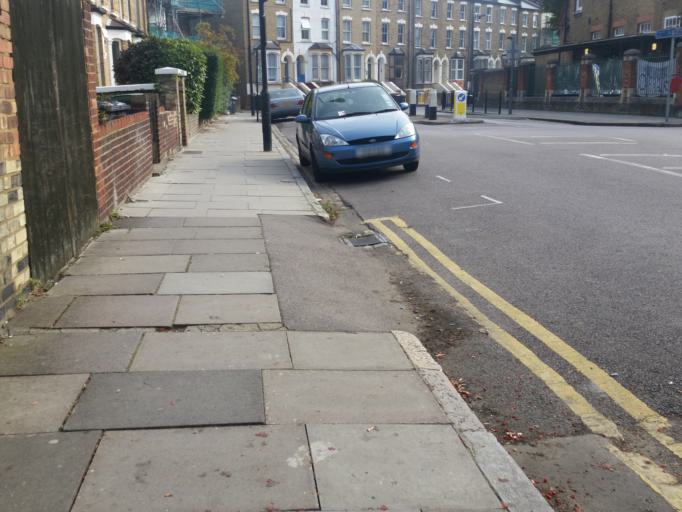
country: GB
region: England
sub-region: Greater London
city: Harringay
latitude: 51.5694
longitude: -0.1073
